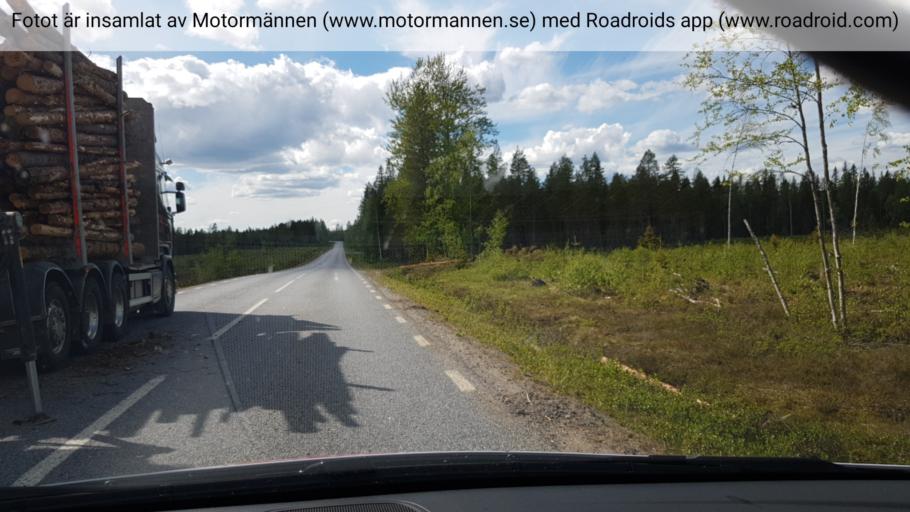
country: SE
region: Vaesterbotten
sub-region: Skelleftea Kommun
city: Burtraesk
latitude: 64.4010
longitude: 20.3508
